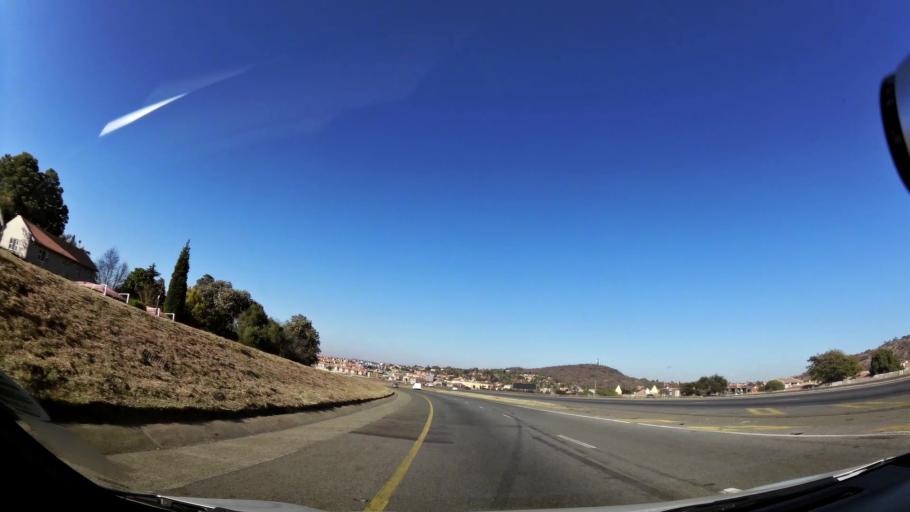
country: ZA
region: Gauteng
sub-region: Ekurhuleni Metropolitan Municipality
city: Germiston
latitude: -26.2828
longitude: 28.1019
